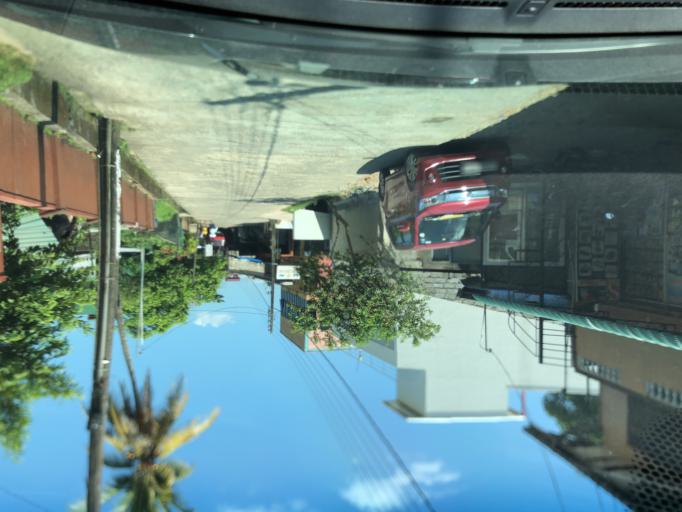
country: LK
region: Western
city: Horana South
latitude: 6.7179
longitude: 80.0605
